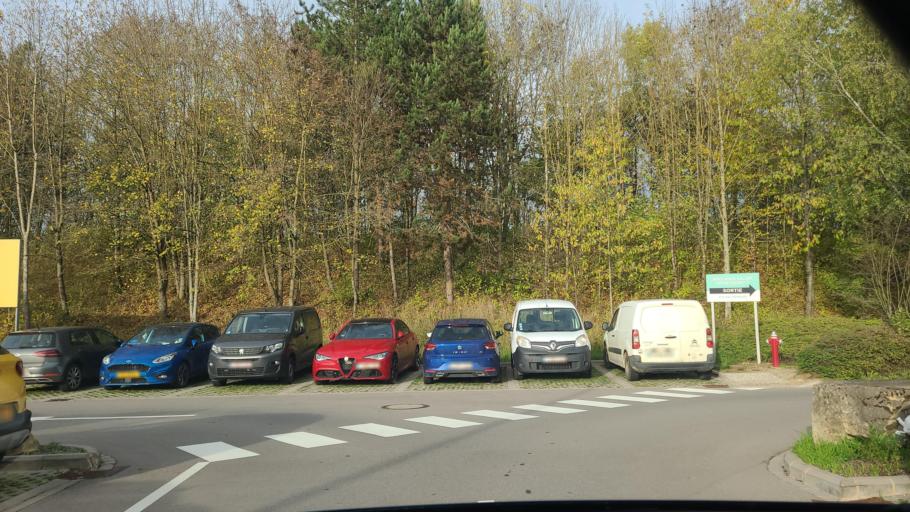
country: LU
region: Luxembourg
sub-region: Canton de Luxembourg
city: Strassen
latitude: 49.6188
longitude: 6.0942
